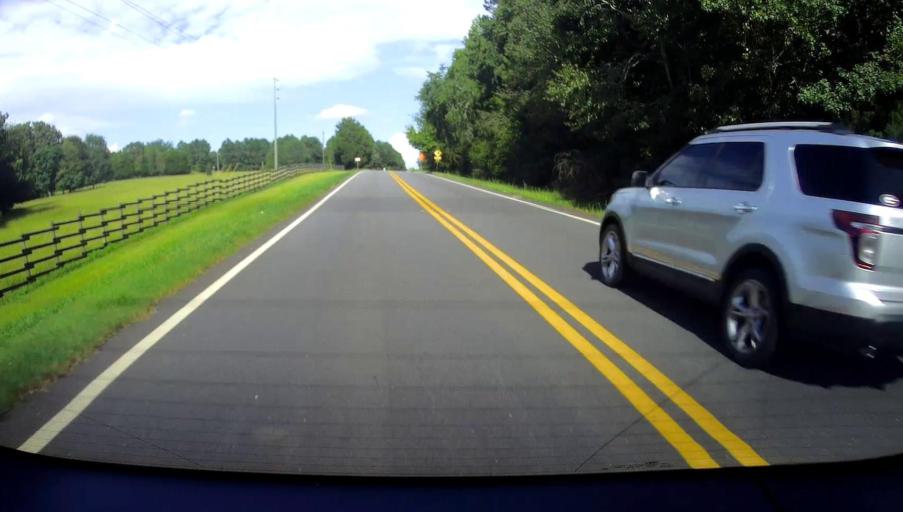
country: US
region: Georgia
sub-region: Upson County
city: Hannahs Mill
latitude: 32.8989
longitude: -84.3889
